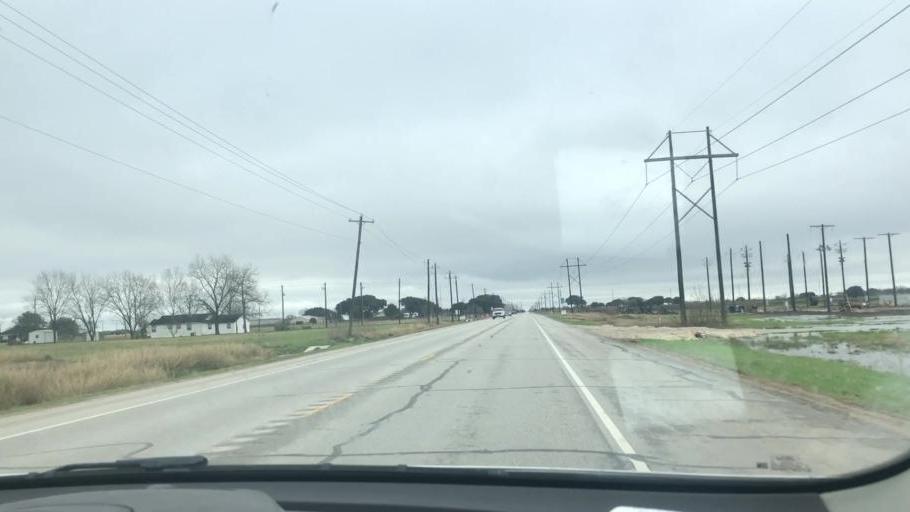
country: US
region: Texas
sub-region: Wharton County
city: Boling
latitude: 29.2070
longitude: -96.0243
